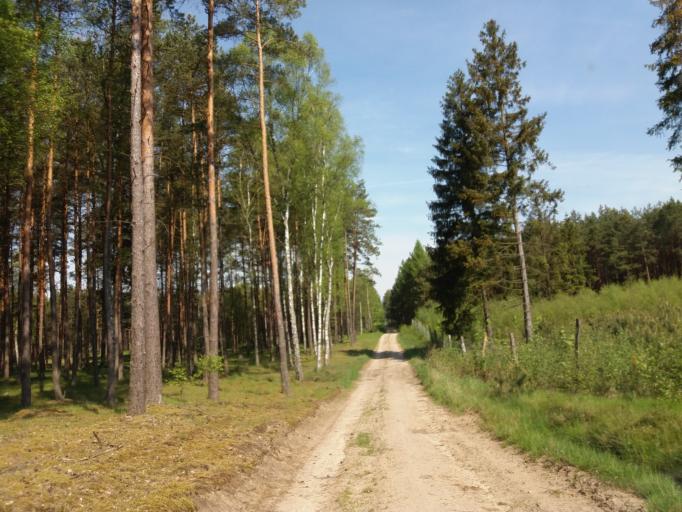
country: PL
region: West Pomeranian Voivodeship
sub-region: Powiat choszczenski
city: Bierzwnik
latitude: 53.1098
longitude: 15.7115
